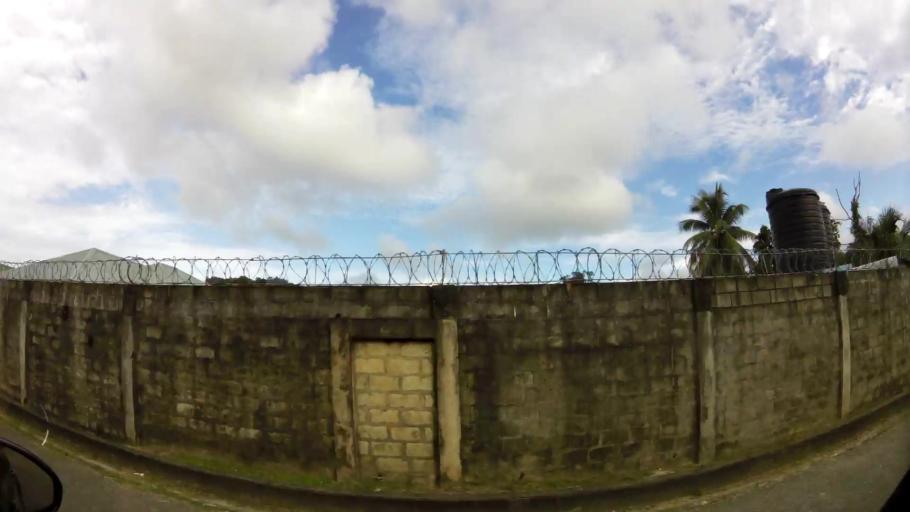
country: TT
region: Diego Martin
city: Petit Valley
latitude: 10.7134
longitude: -61.4785
